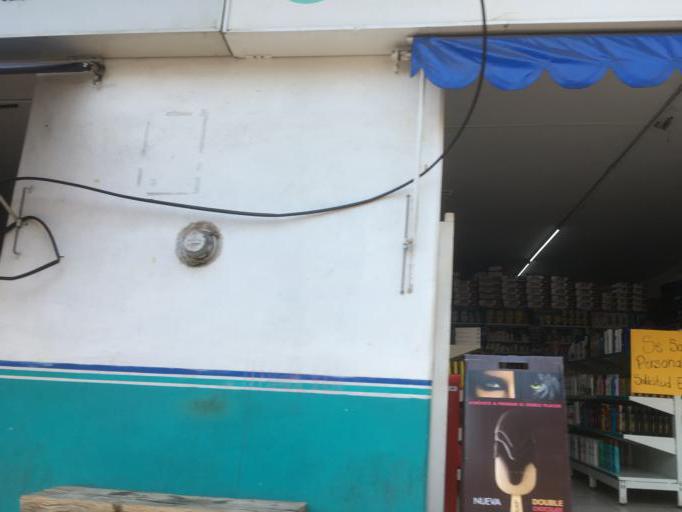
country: MX
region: Michoacan
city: Quiroga
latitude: 19.6624
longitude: -101.5255
